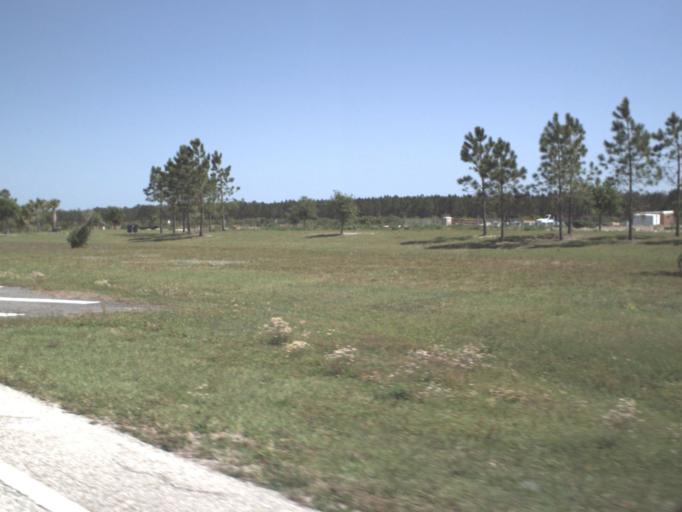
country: US
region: Florida
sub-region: Flagler County
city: Palm Coast
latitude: 29.5807
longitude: -81.2777
